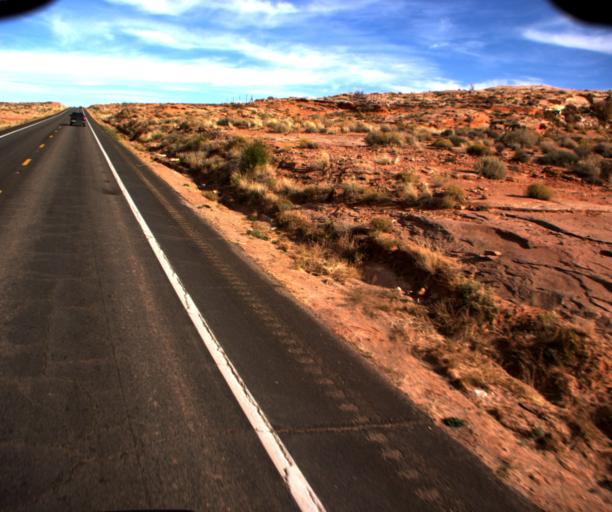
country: US
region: Arizona
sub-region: Apache County
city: Many Farms
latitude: 36.9245
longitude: -109.6012
